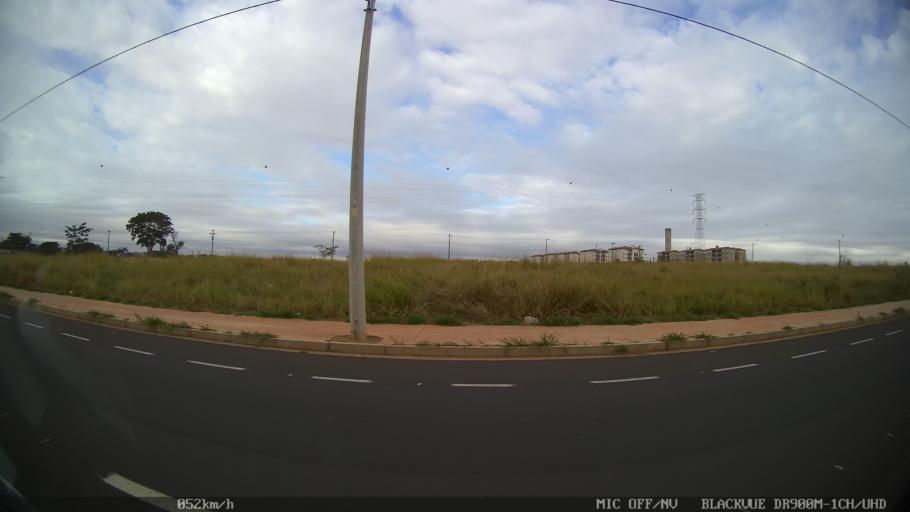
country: BR
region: Sao Paulo
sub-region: Sao Jose Do Rio Preto
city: Sao Jose do Rio Preto
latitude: -20.8405
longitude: -49.4167
